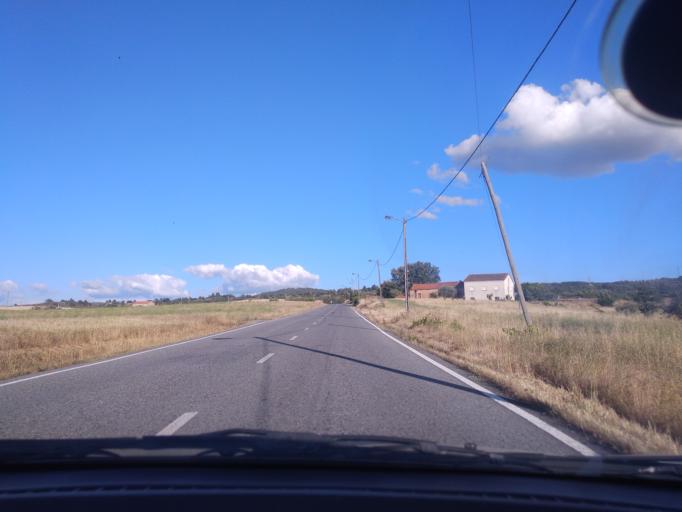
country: PT
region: Castelo Branco
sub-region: Covilha
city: Teixoso
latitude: 40.2508
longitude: -7.3982
